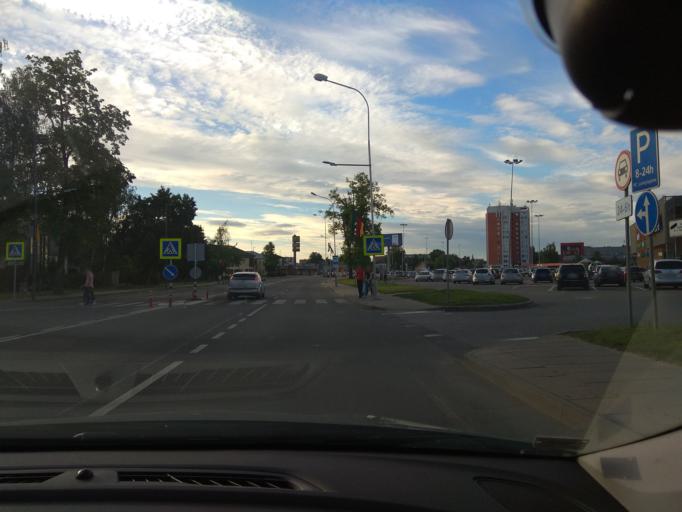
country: LT
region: Marijampoles apskritis
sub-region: Marijampole Municipality
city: Marijampole
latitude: 54.5589
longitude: 23.3542
